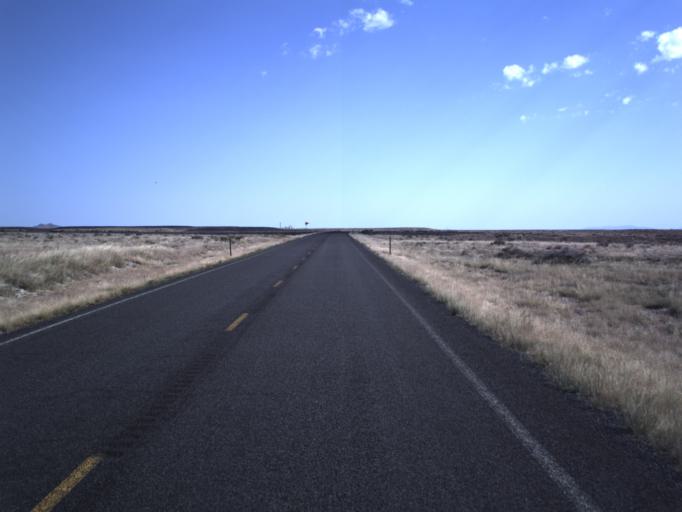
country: US
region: Utah
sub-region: Millard County
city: Fillmore
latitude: 38.8808
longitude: -112.8319
